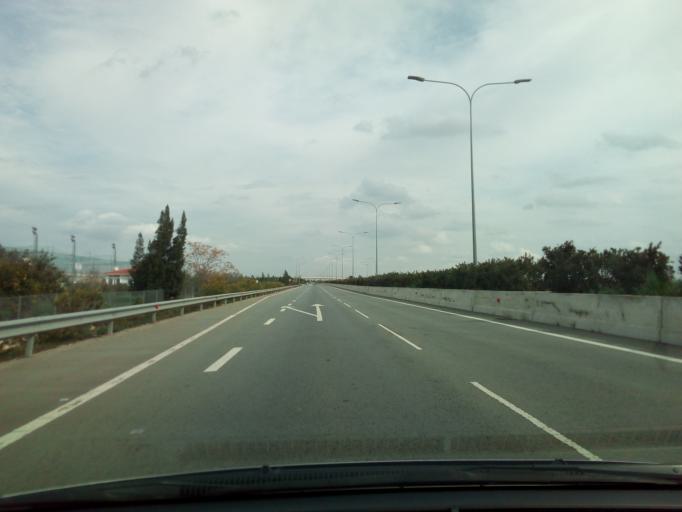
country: CY
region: Lefkosia
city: Kokkinotrimithia
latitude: 35.1603
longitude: 33.1966
